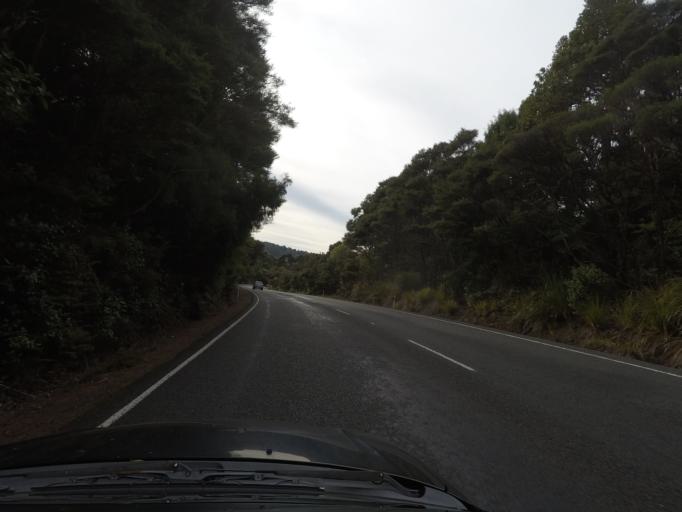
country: NZ
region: Auckland
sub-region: Auckland
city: Titirangi
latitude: -36.9397
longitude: 174.5546
